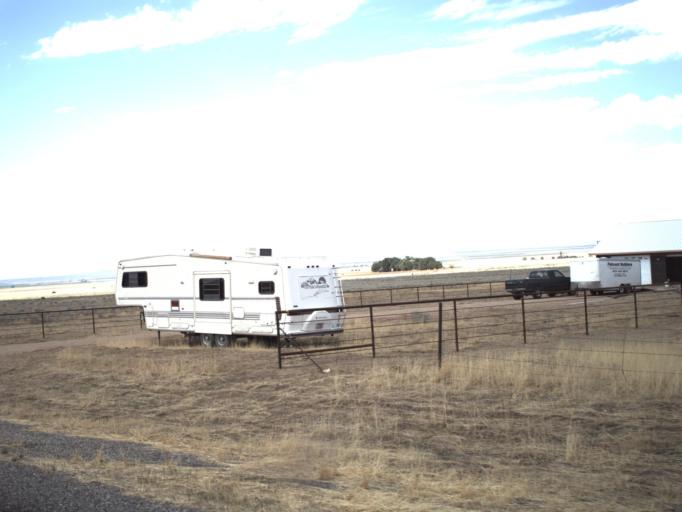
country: US
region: Utah
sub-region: Millard County
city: Fillmore
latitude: 39.1417
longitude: -112.2401
